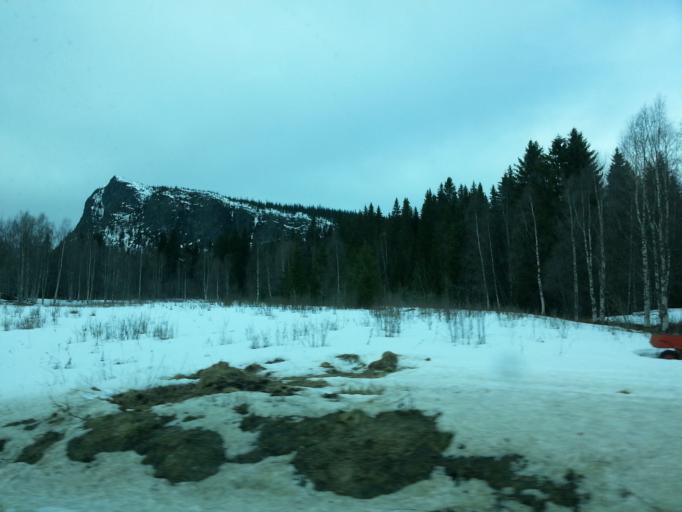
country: NO
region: Nord-Trondelag
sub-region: Lierne
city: Sandvika
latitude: 64.3941
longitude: 14.4833
